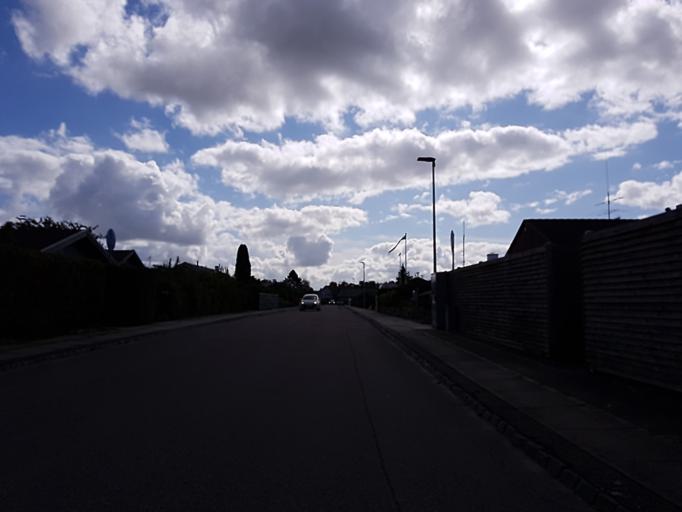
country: DK
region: Capital Region
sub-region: Egedal Kommune
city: Olstykke
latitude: 55.7907
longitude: 12.1440
